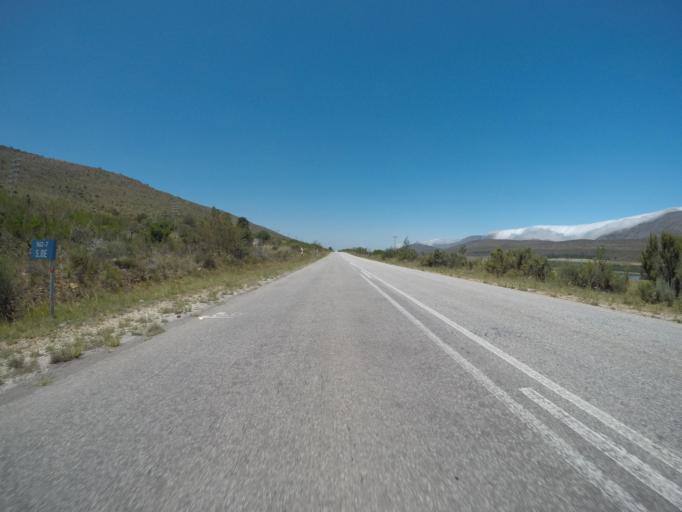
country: ZA
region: Eastern Cape
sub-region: Cacadu District Municipality
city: Kareedouw
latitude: -33.8365
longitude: 23.9176
